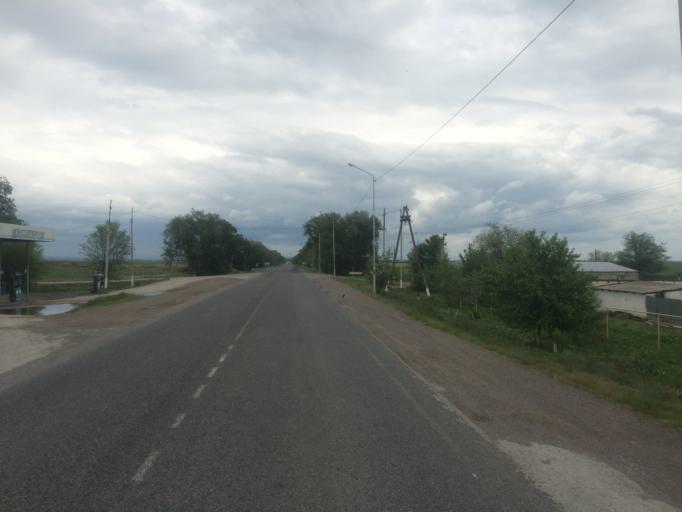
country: KZ
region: Zhambyl
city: Georgiyevka
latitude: 43.2265
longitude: 74.4031
